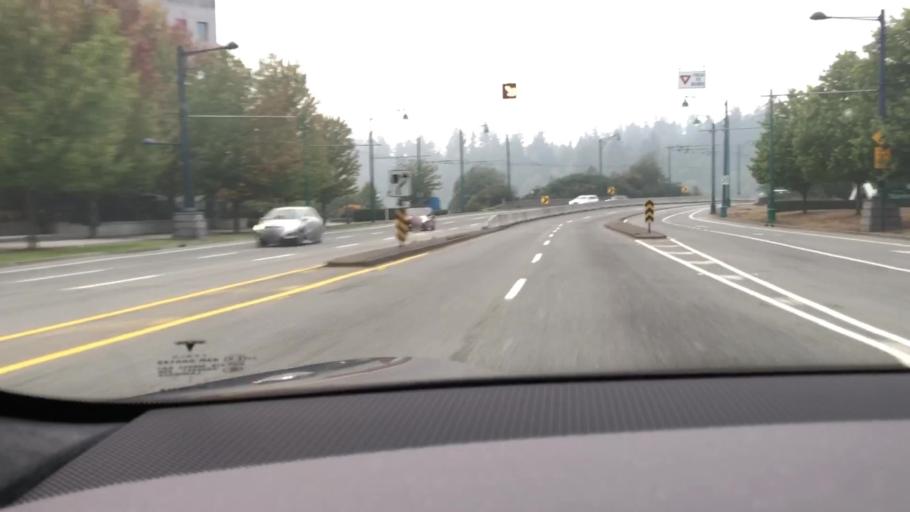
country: CA
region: British Columbia
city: West End
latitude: 49.2940
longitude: -123.1360
